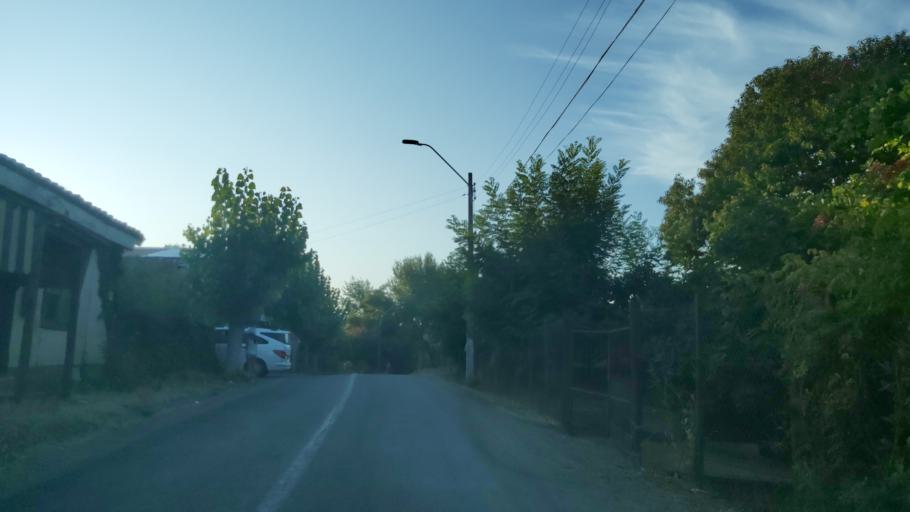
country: CL
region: Biobio
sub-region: Provincia de Biobio
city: La Laja
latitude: -37.1627
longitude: -72.9134
